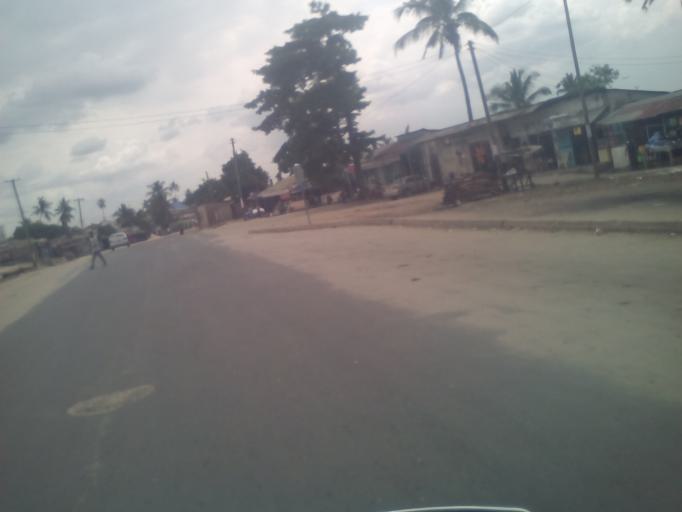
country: TZ
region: Dar es Salaam
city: Dar es Salaam
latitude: -6.8739
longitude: 39.2238
